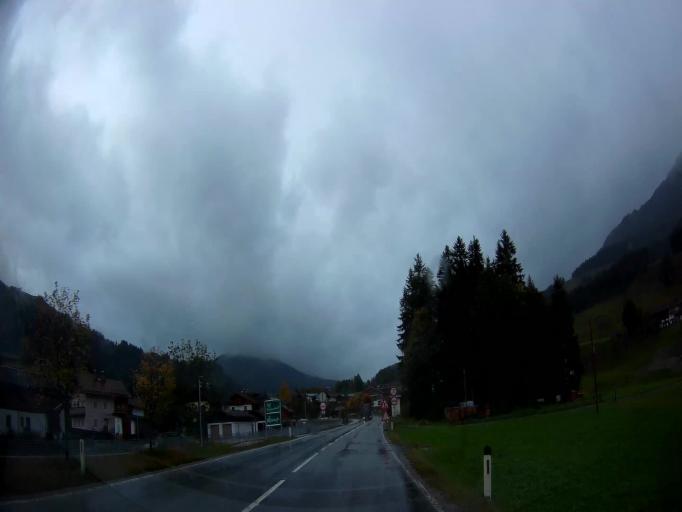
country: AT
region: Salzburg
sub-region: Politischer Bezirk Zell am See
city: Leogang
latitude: 47.4405
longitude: 12.7321
